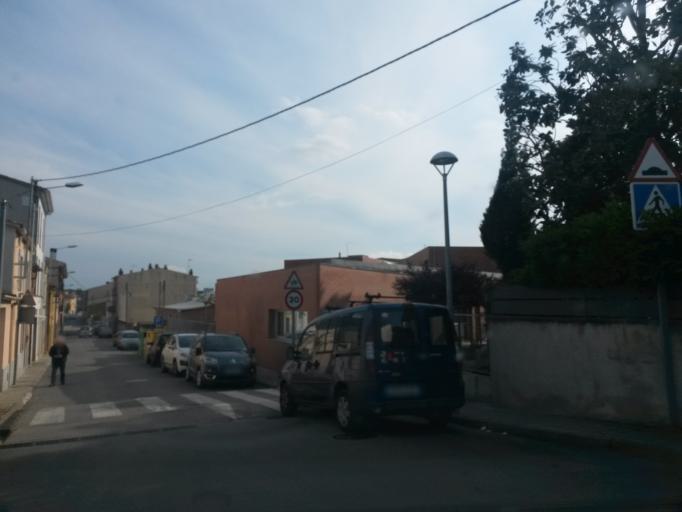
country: ES
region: Catalonia
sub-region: Provincia de Girona
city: Caldes de Malavella
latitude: 41.8418
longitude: 2.8099
